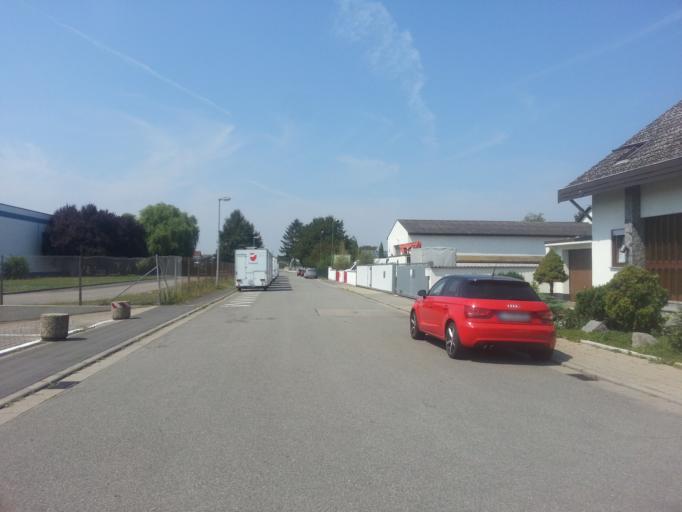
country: DE
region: Baden-Wuerttemberg
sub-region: Karlsruhe Region
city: Edingen-Neckarhausen
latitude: 49.4540
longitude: 8.5973
